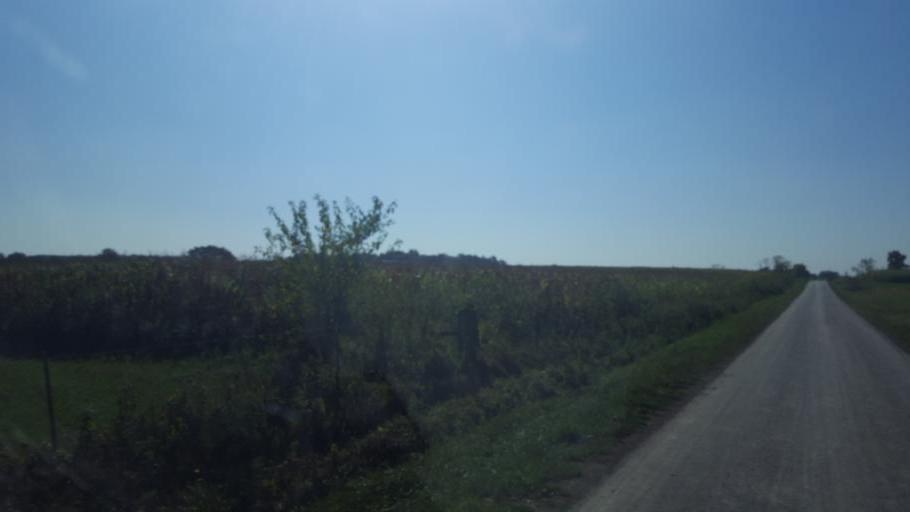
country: US
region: Ohio
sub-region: Union County
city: Richwood
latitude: 40.5434
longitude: -83.4135
